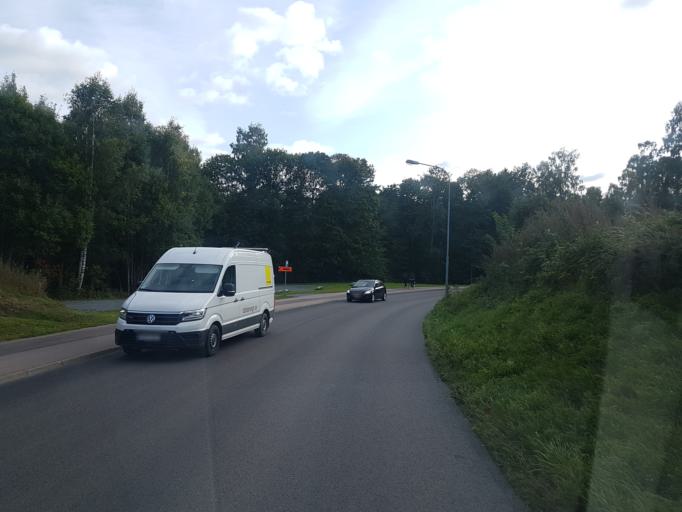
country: SE
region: Dalarna
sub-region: Saters Kommun
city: Saeter
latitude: 60.3499
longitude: 15.7520
